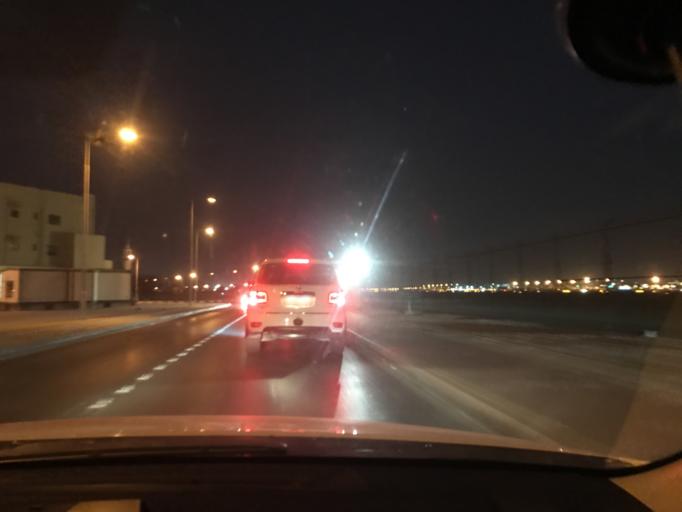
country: BH
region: Muharraq
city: Al Muharraq
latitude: 26.2821
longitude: 50.6176
